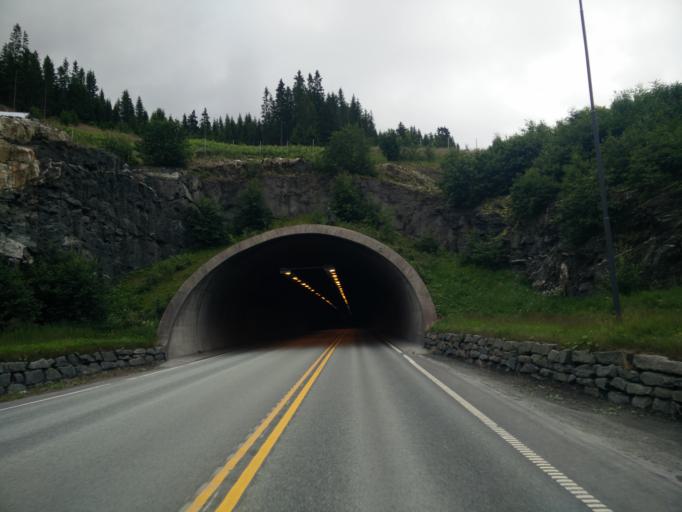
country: NO
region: Sor-Trondelag
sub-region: Skaun
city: Borsa
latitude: 63.3289
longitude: 10.0006
